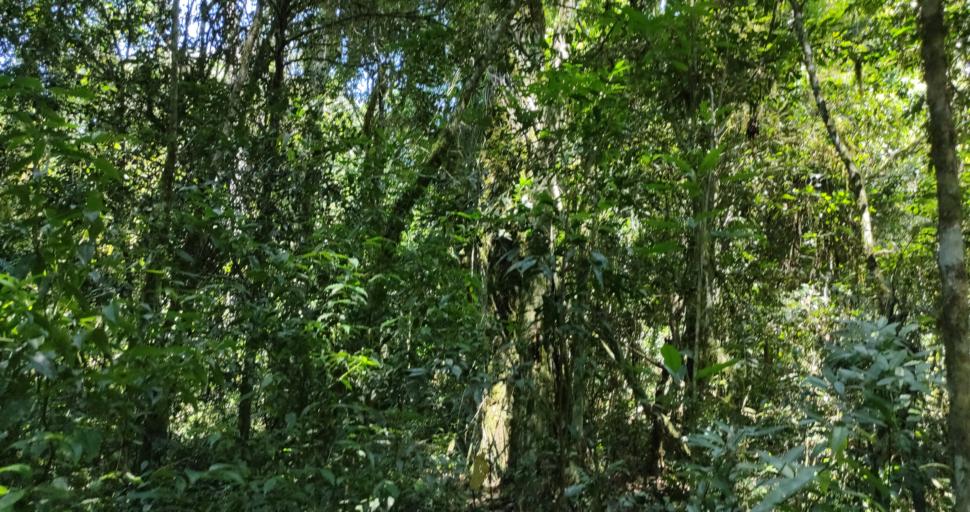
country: BR
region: Rio Grande do Sul
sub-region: Tres Passos
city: Tres Passos
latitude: -27.1476
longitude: -53.8977
